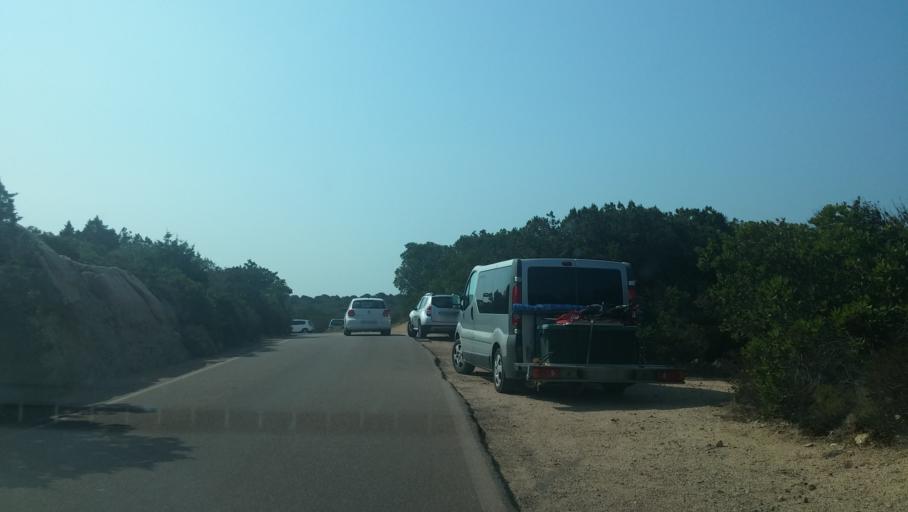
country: IT
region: Sardinia
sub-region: Provincia di Olbia-Tempio
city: La Maddalena
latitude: 41.1890
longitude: 9.4562
